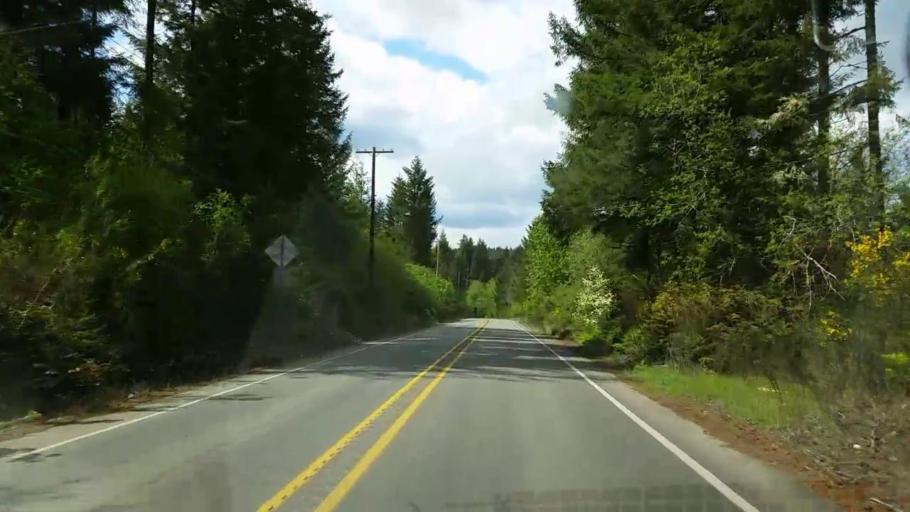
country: US
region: Washington
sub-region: Pierce County
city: Key Center
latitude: 47.3733
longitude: -122.7743
